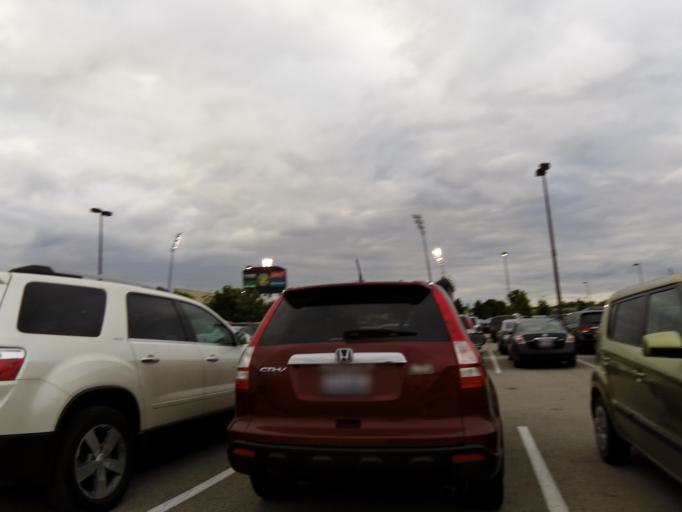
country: US
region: Ohio
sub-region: Franklin County
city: Columbus
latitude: 40.0068
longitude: -82.9903
